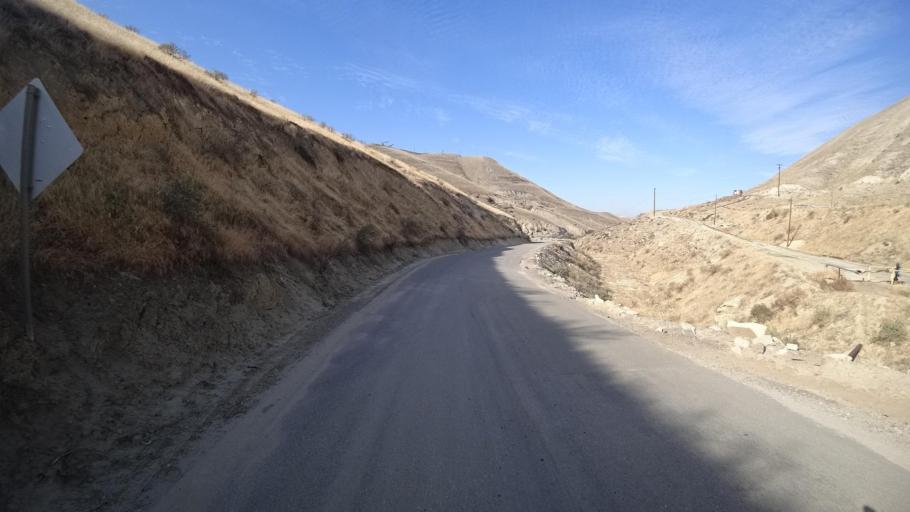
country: US
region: California
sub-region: Kern County
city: Oildale
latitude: 35.5000
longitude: -118.9003
